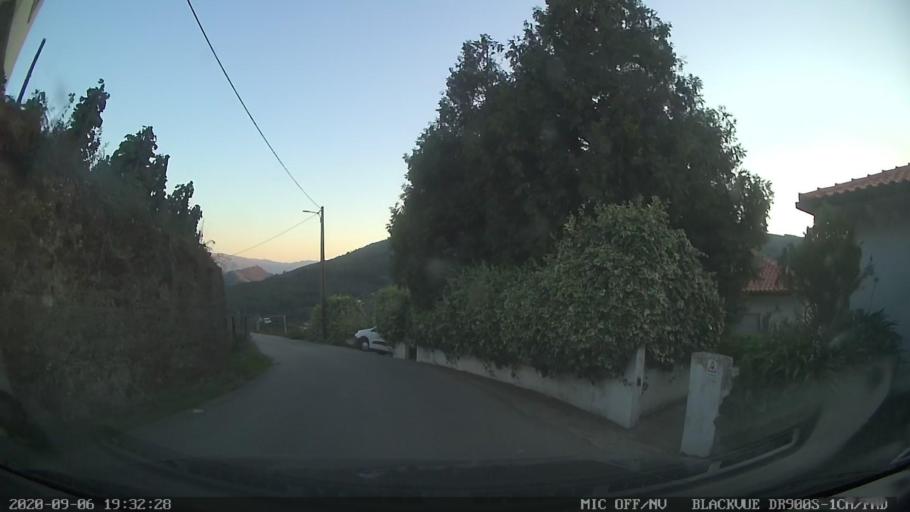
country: PT
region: Vila Real
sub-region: Mesao Frio
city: Mesao Frio
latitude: 41.1790
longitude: -7.9023
